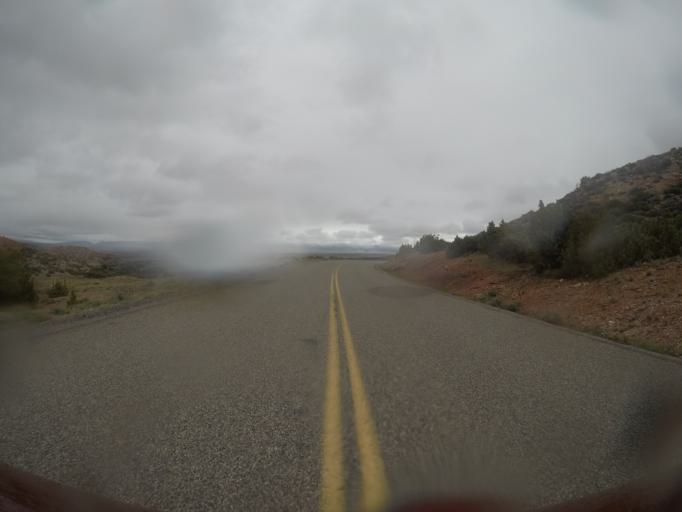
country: US
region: Wyoming
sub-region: Big Horn County
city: Lovell
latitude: 45.0255
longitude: -108.2612
